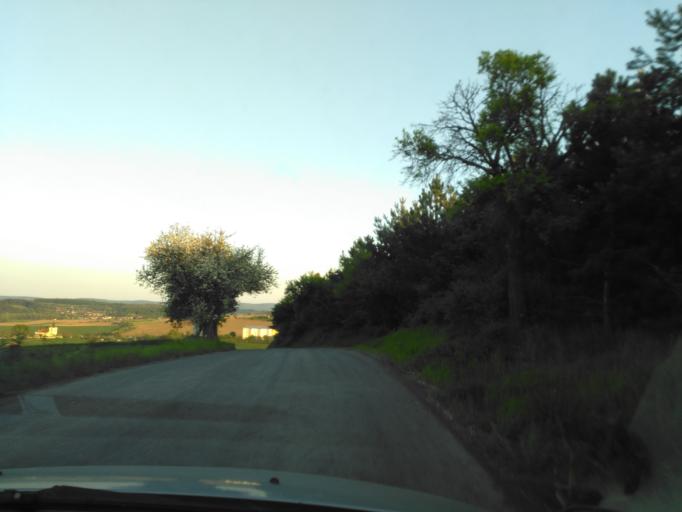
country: CZ
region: Central Bohemia
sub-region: Okres Beroun
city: Kraluv Dvur
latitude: 49.9131
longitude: 14.0334
